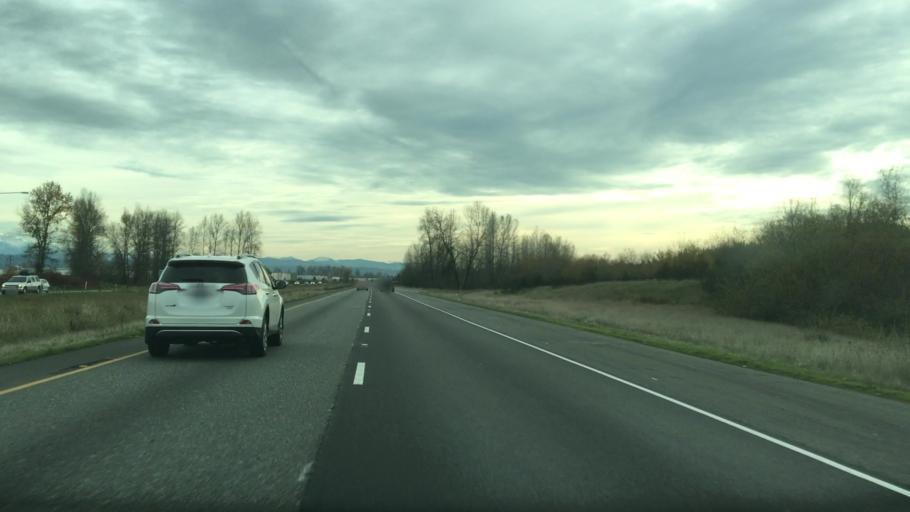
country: US
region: Washington
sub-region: Pierce County
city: Sumner
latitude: 47.2327
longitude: -122.2508
